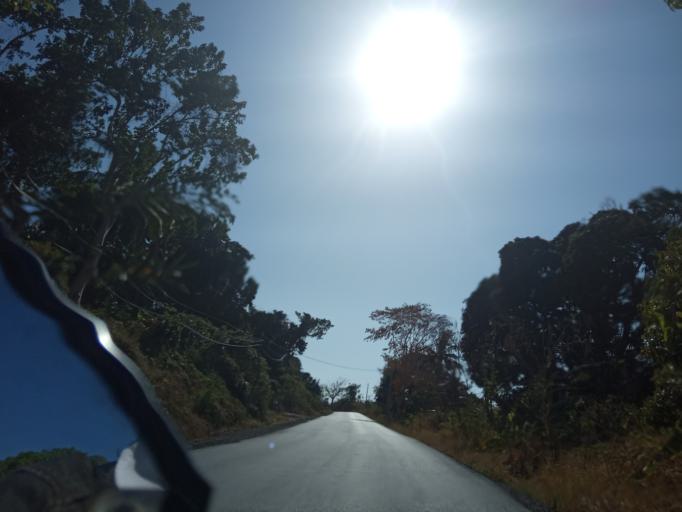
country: YT
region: Bandrele
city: Bandrele
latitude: -12.8918
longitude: 45.2069
